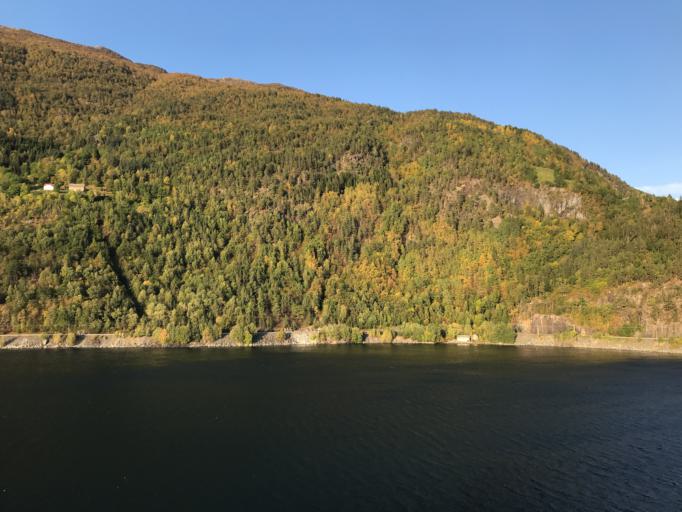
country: NO
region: Sogn og Fjordane
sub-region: Gloppen
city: Sandane
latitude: 61.8453
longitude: 6.1261
